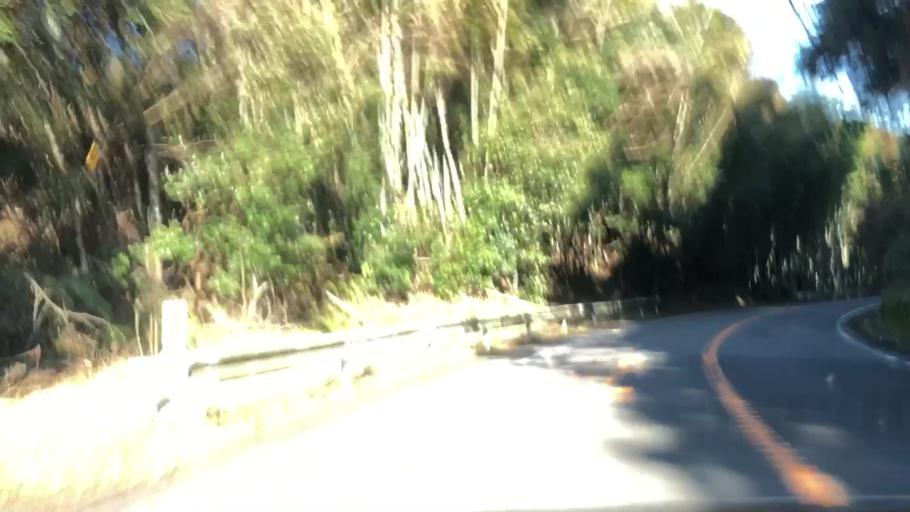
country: JP
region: Kagoshima
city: Satsumasendai
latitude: 31.8569
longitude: 130.4298
